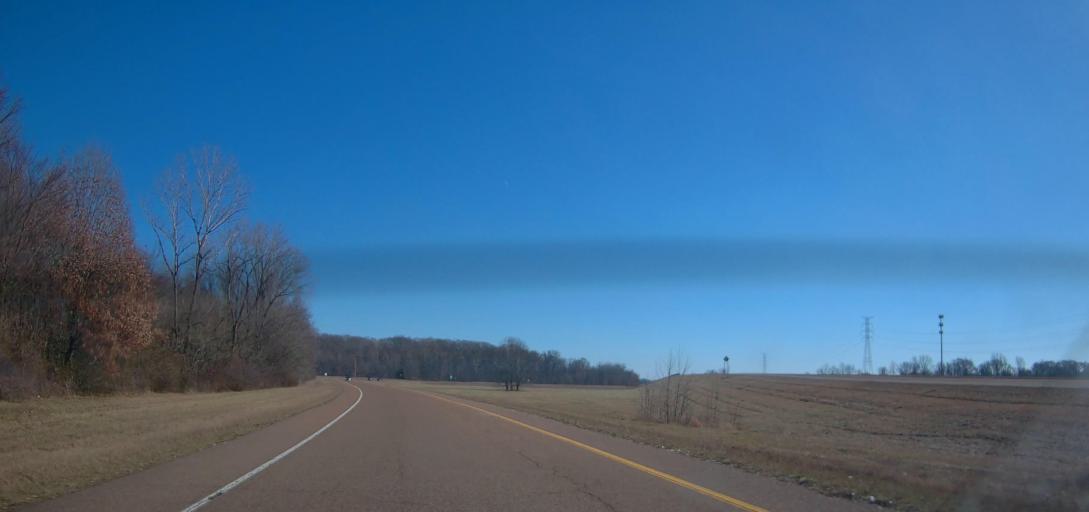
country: US
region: Tennessee
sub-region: Shelby County
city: Millington
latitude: 35.3215
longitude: -89.8761
